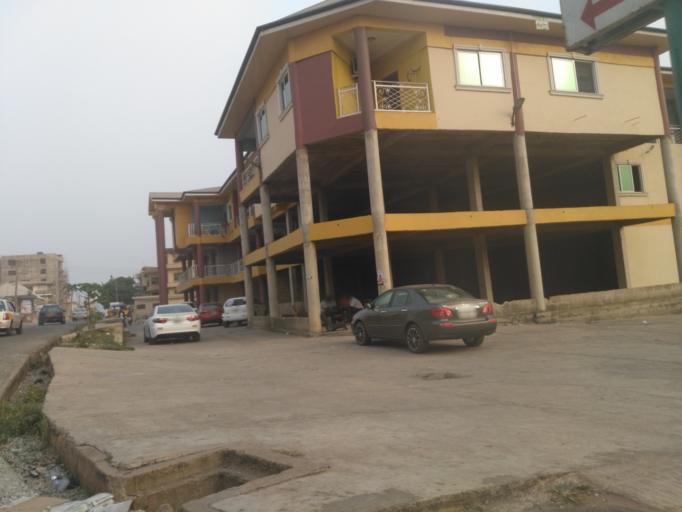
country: GH
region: Ashanti
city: Kumasi
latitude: 6.7104
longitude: -1.6166
